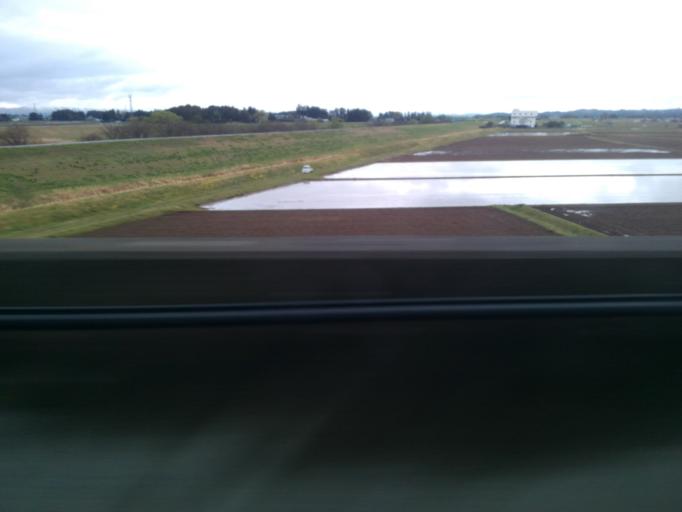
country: JP
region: Miyagi
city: Furukawa
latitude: 38.5412
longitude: 140.9614
